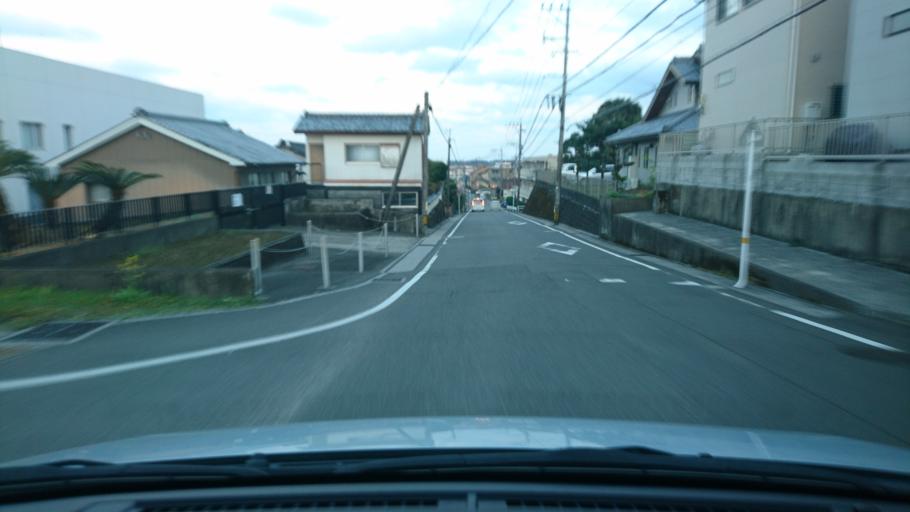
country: JP
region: Miyazaki
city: Miyazaki-shi
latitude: 31.8607
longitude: 131.4294
